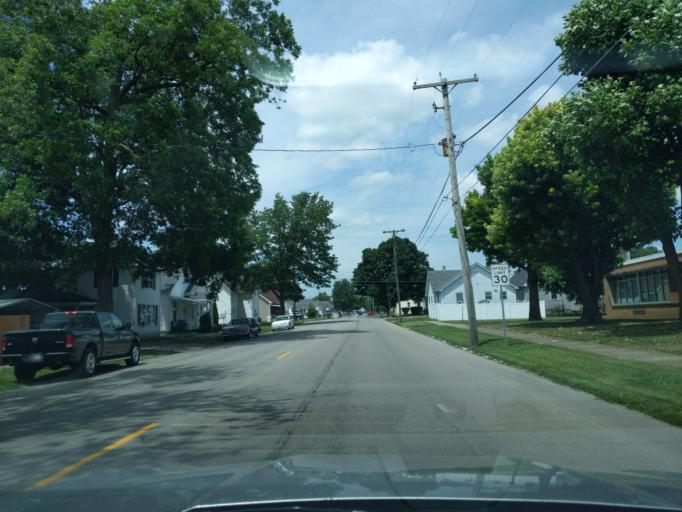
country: US
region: Indiana
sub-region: Decatur County
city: Greensburg
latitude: 39.3379
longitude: -85.4890
